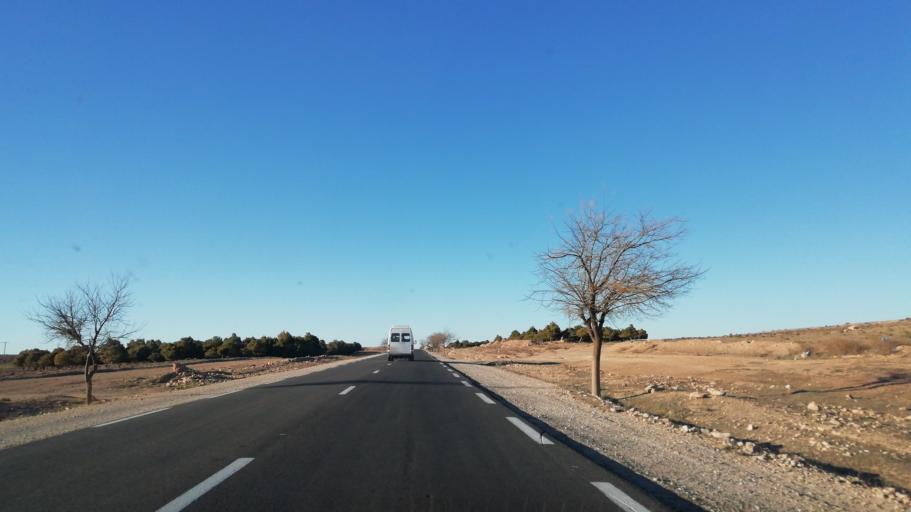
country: DZ
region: Tlemcen
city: Sebdou
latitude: 34.5276
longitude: -1.2933
